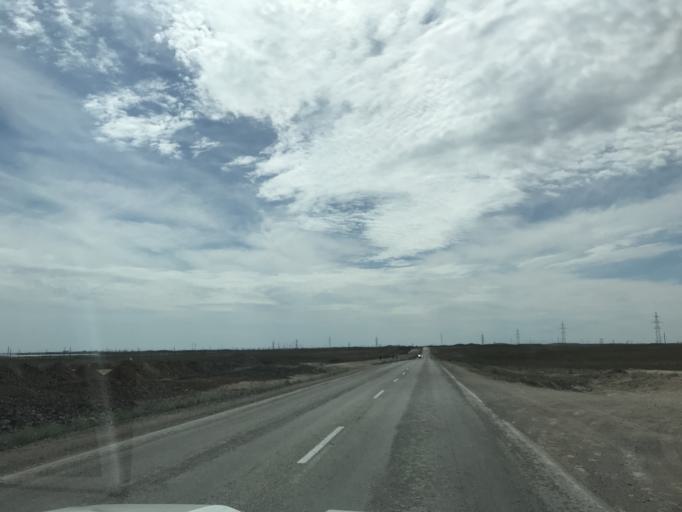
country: KZ
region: Almaty Oblysy
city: Ulken
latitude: 45.2210
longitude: 73.8593
